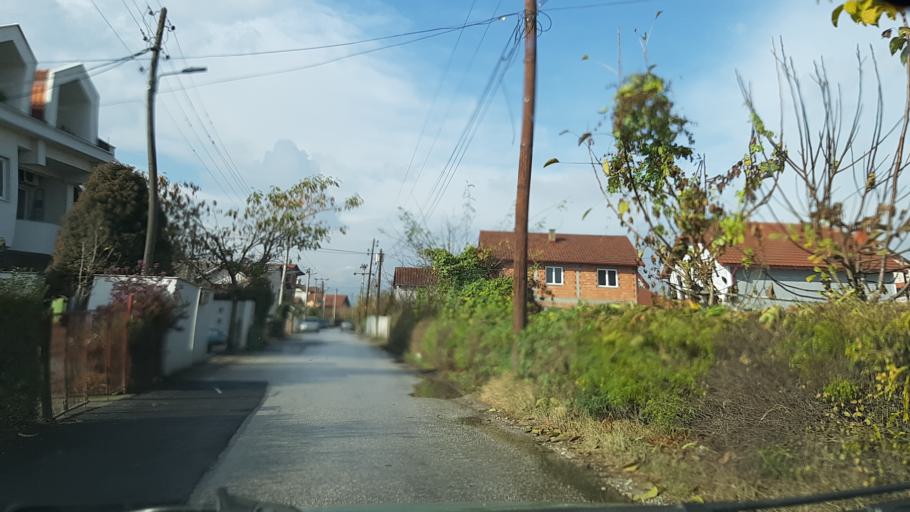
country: MK
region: Kisela Voda
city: Kisela Voda
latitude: 41.9824
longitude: 21.4897
